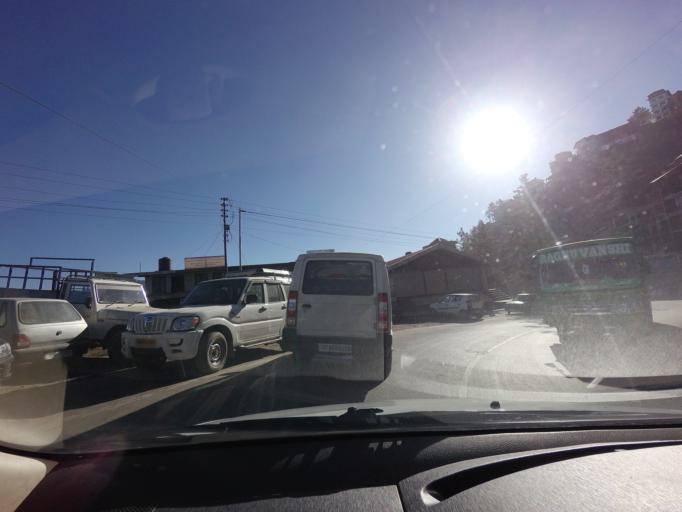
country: IN
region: Himachal Pradesh
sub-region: Shimla
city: Shimla
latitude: 31.1090
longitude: 77.2073
